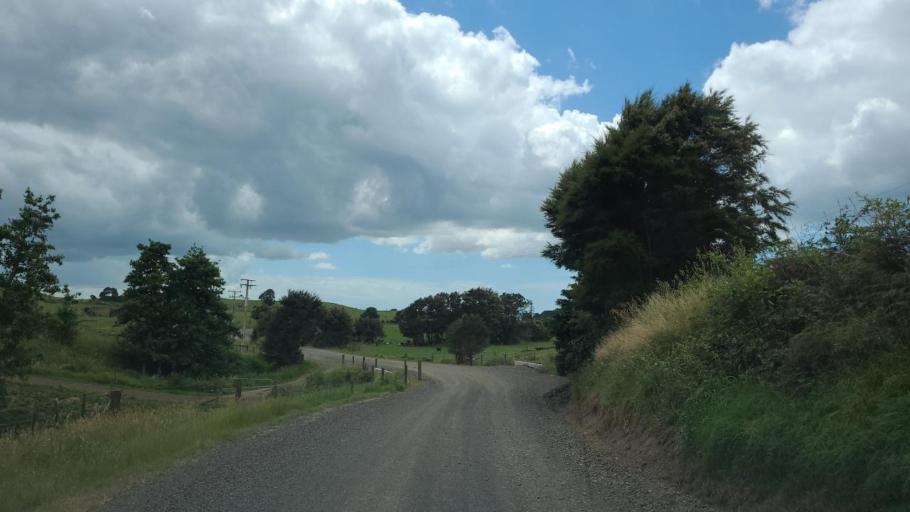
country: NZ
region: Waikato
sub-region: Hauraki District
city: Ngatea
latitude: -37.4521
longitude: 175.5004
